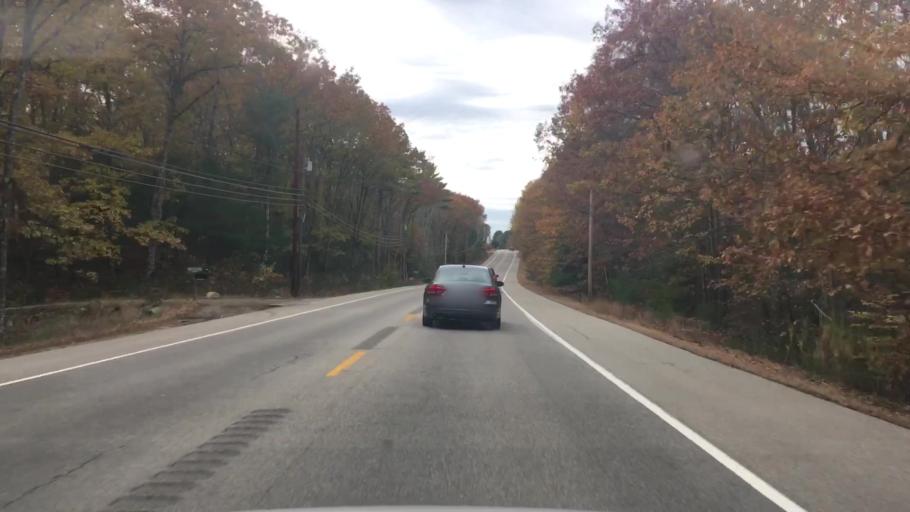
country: US
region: Maine
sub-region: York County
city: Alfred
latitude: 43.4762
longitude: -70.6687
